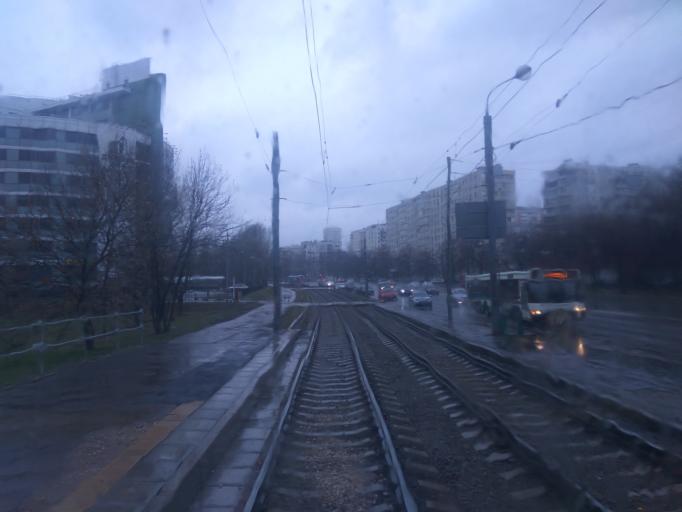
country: RU
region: Moscow
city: Leonovo
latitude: 55.8715
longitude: 37.6514
